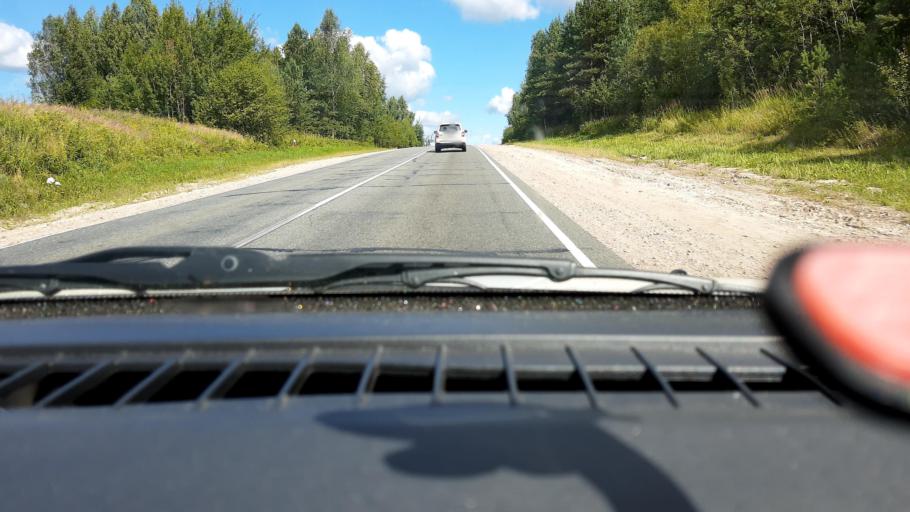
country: RU
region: Nizjnij Novgorod
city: Arzamas
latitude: 55.3898
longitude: 43.9173
